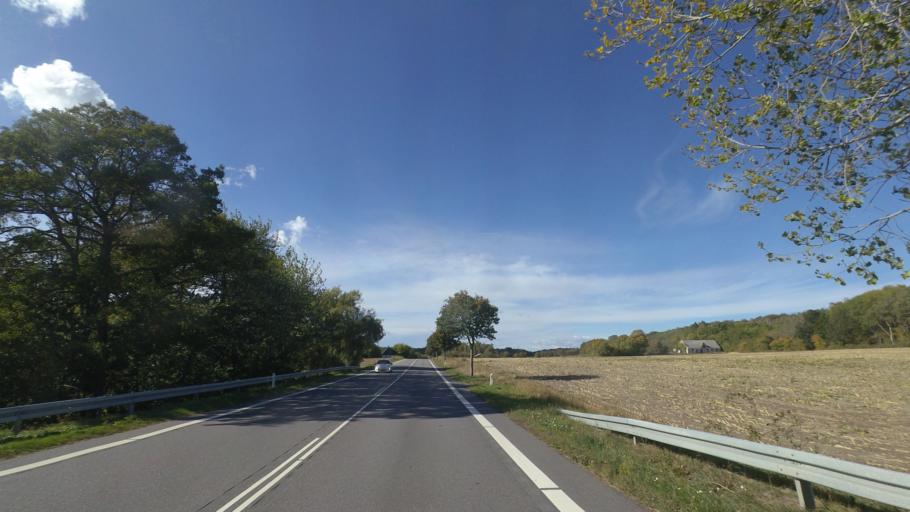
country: DK
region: Capital Region
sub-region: Bornholm Kommune
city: Ronne
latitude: 55.0781
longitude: 14.7671
